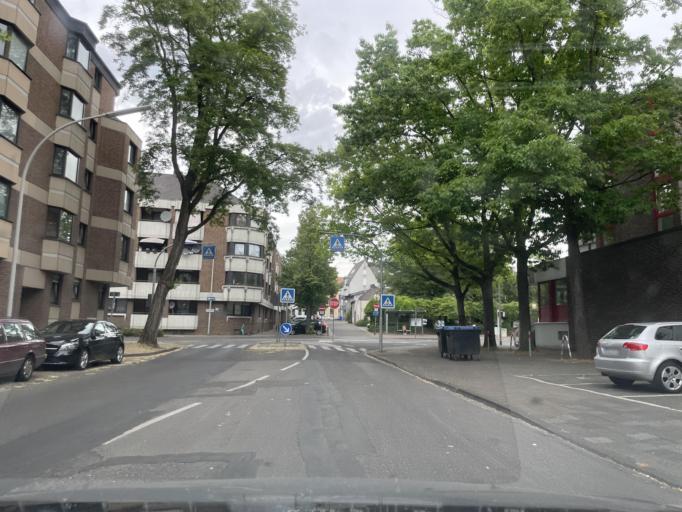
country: DE
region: North Rhine-Westphalia
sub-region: Regierungsbezirk Dusseldorf
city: Monchengladbach
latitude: 51.1686
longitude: 6.4519
